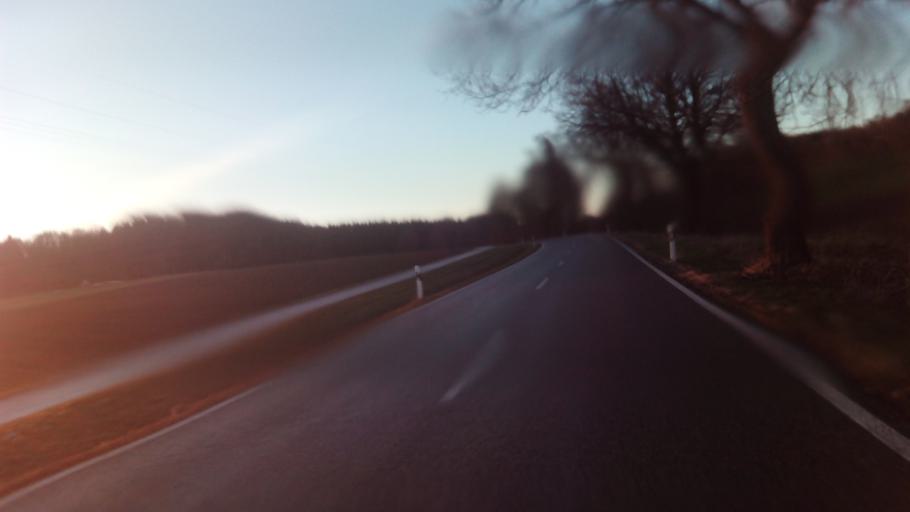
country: DE
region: Baden-Wuerttemberg
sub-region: Tuebingen Region
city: Oberdischingen
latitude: 48.3333
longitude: 9.8436
